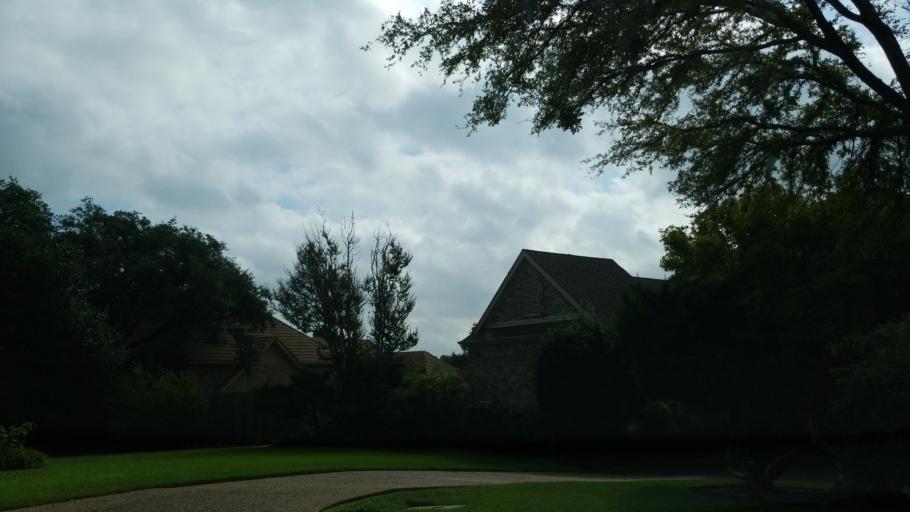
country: US
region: Texas
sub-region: Dallas County
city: Addison
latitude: 32.9430
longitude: -96.7997
